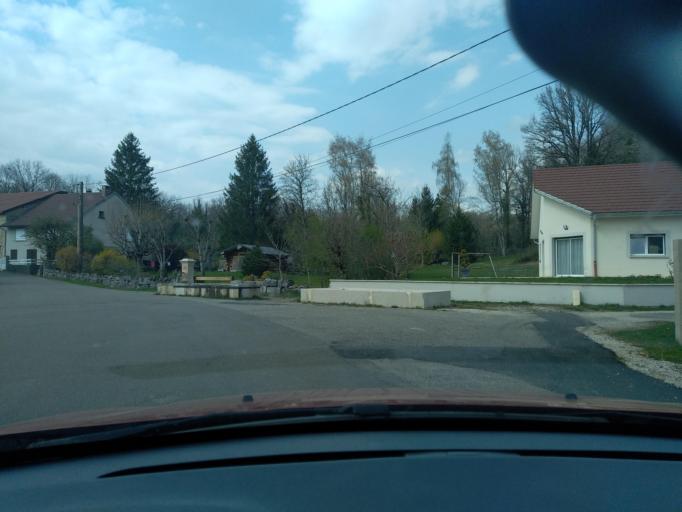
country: FR
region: Franche-Comte
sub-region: Departement du Jura
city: Moirans-en-Montagne
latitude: 46.4570
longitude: 5.7391
